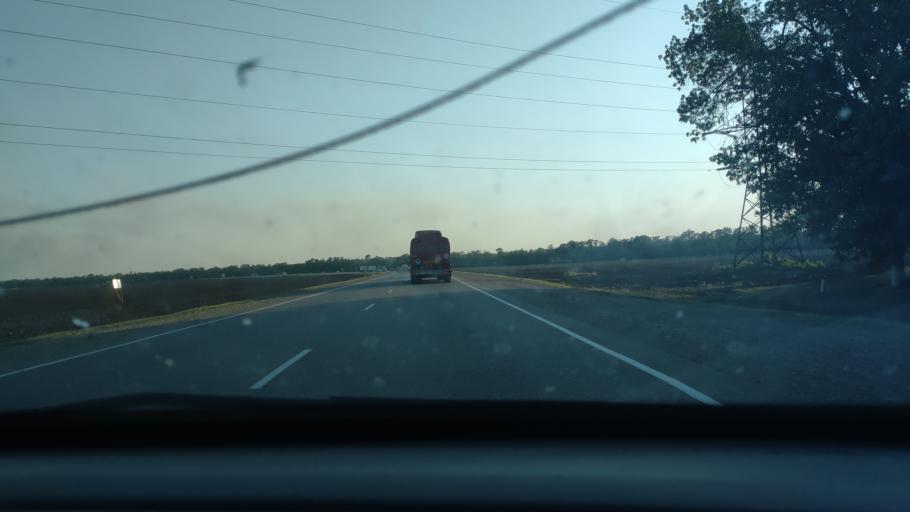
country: RU
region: Krasnodarskiy
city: Kanevskaya
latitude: 46.0307
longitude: 38.9759
